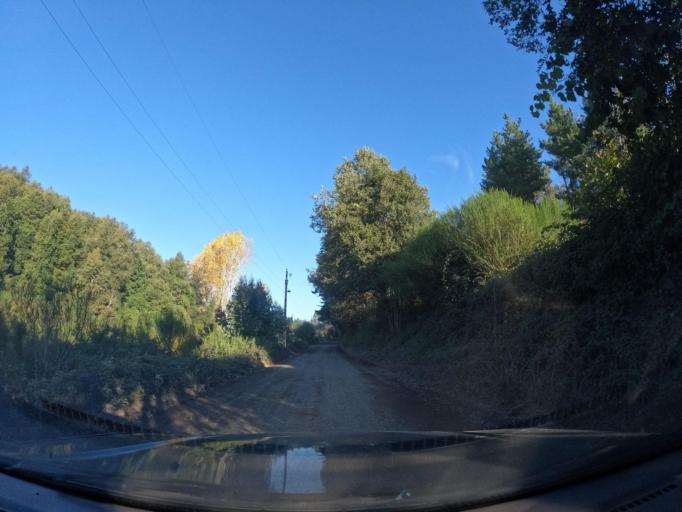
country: CL
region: Biobio
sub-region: Provincia de Concepcion
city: Chiguayante
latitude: -37.0289
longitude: -72.8845
